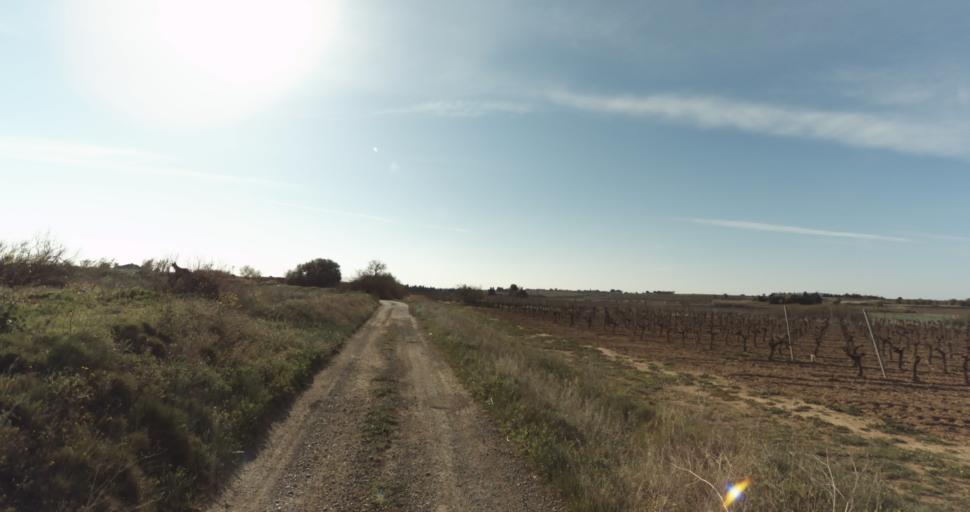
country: FR
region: Languedoc-Roussillon
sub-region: Departement de l'Herault
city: Marseillan
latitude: 43.3612
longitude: 3.5087
